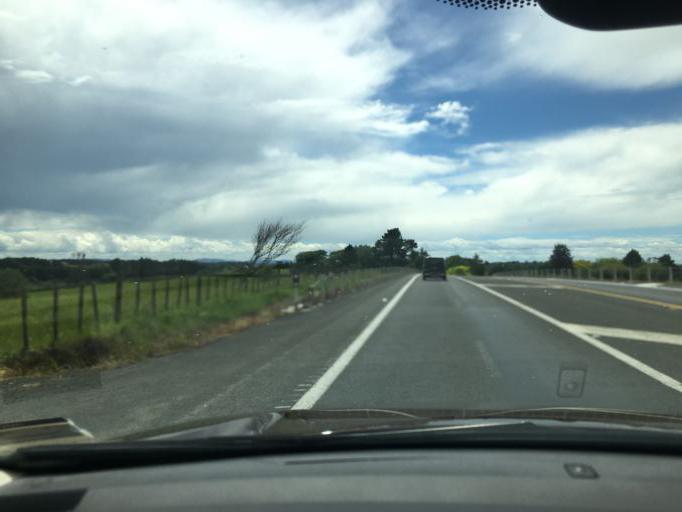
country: NZ
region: Waikato
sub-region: Waipa District
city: Cambridge
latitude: -37.9382
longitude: 175.3146
